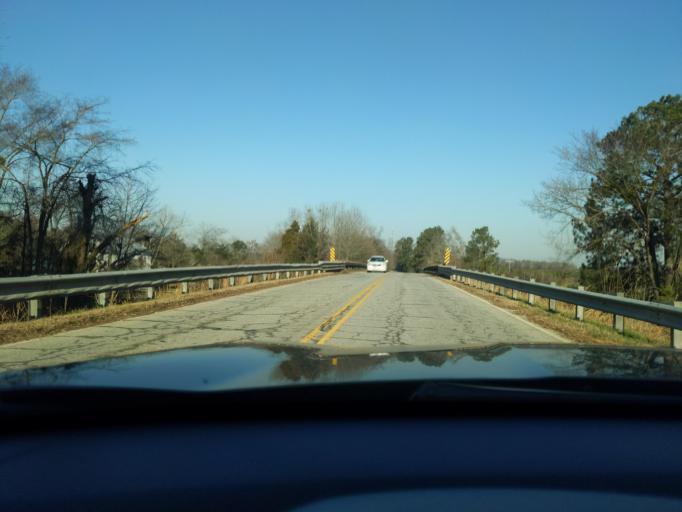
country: US
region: South Carolina
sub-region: Newberry County
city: Newberry
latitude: 34.2196
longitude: -81.7183
